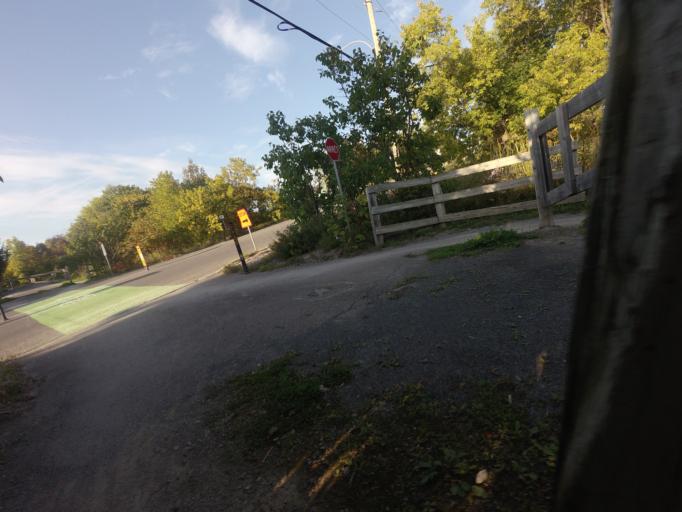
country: CA
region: Quebec
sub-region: Laurentides
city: Prevost
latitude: 45.8503
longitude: -74.0651
